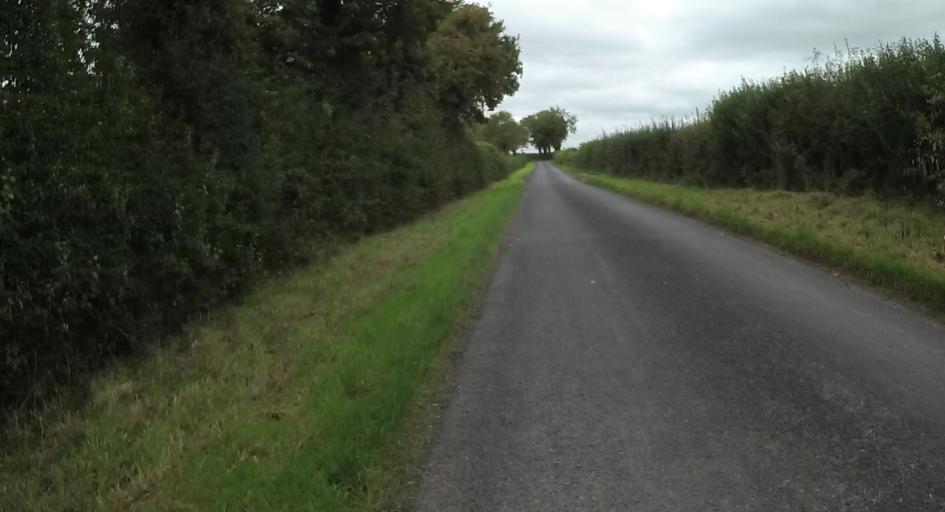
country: GB
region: England
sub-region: Hampshire
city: Four Marks
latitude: 51.1541
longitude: -1.1174
